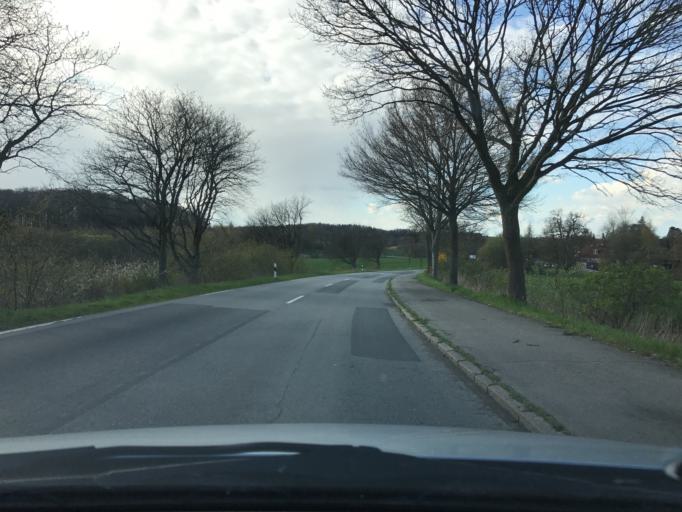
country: DE
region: Schleswig-Holstein
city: Kirchnuchel
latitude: 54.2051
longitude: 10.6748
